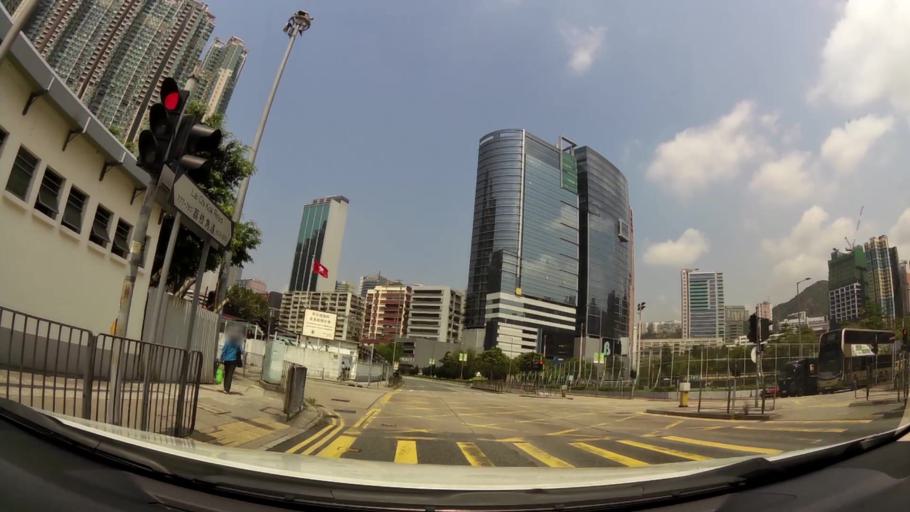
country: HK
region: Sham Shui Po
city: Sham Shui Po
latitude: 22.3352
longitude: 114.1518
